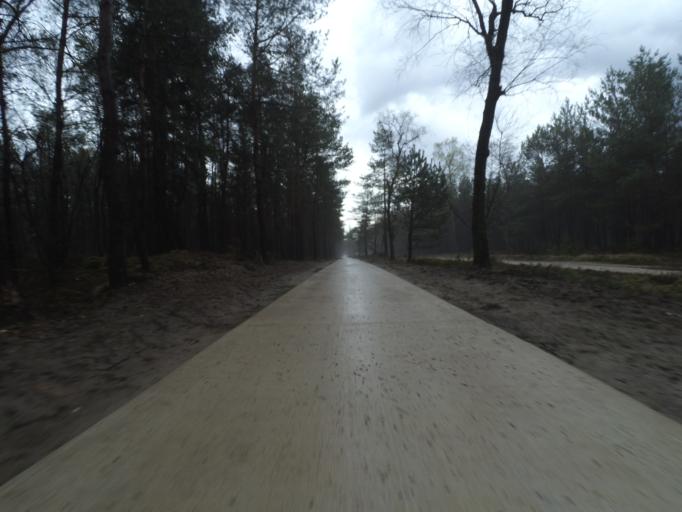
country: NL
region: Gelderland
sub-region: Gemeente Apeldoorn
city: Beekbergen
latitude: 52.1442
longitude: 5.8999
